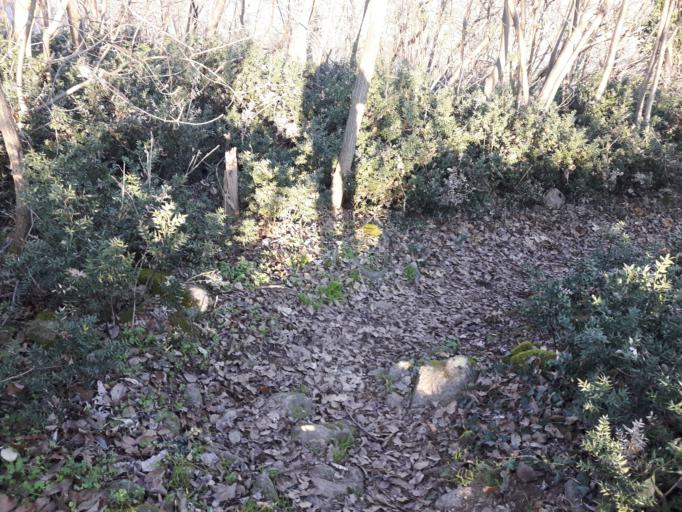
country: IT
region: Veneto
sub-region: Provincia di Padova
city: San Biagio
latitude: 45.3680
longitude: 11.7564
